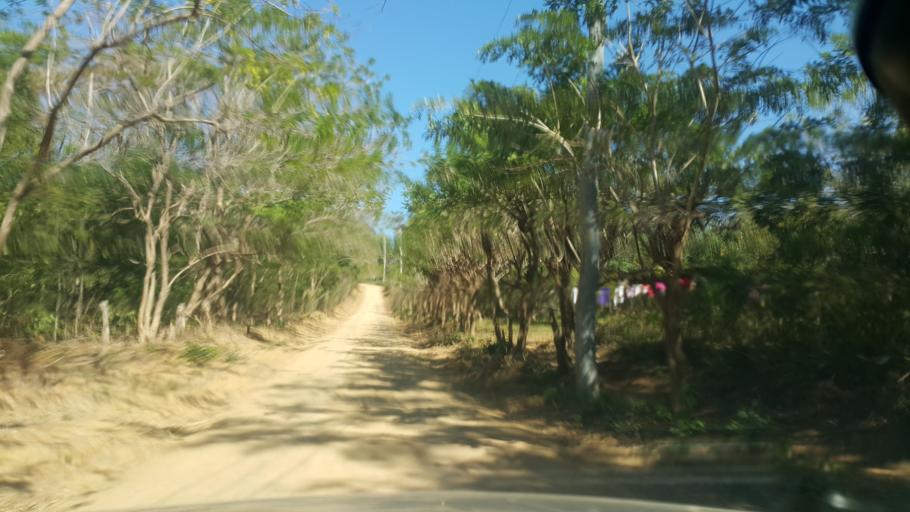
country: NI
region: Rivas
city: San Juan del Sur
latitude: 11.2830
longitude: -85.8792
